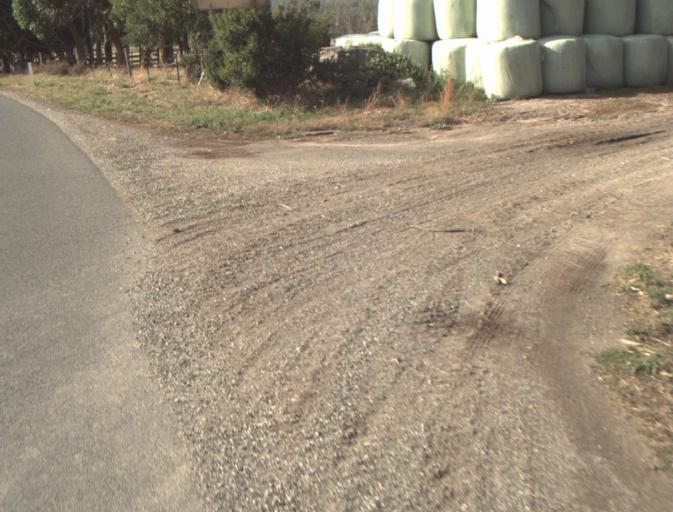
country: AU
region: Tasmania
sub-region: Launceston
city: Mayfield
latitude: -41.2284
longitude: 147.1230
